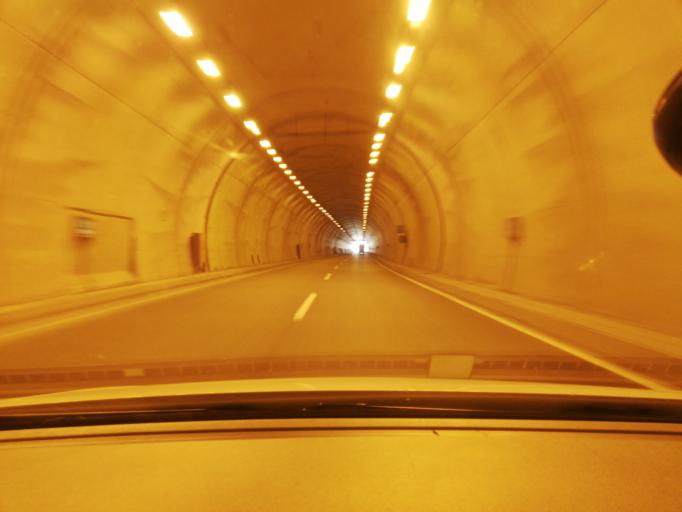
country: TR
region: Zonguldak
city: Alapli
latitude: 41.1659
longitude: 31.3632
